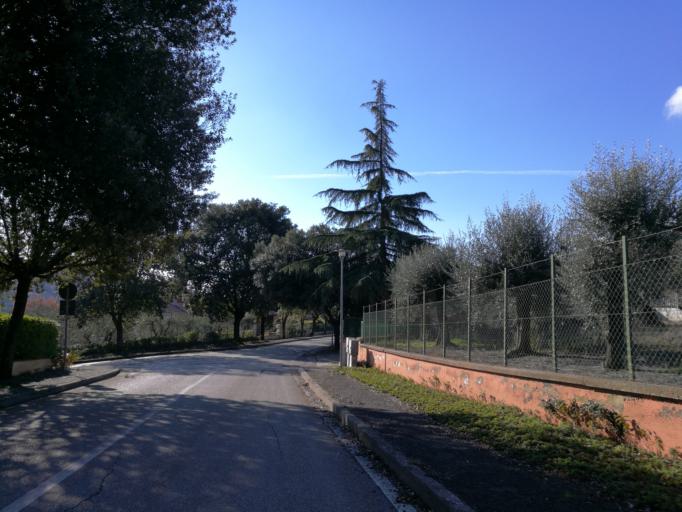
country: IT
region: Umbria
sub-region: Provincia di Perugia
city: Perugia
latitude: 43.0806
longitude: 12.3756
